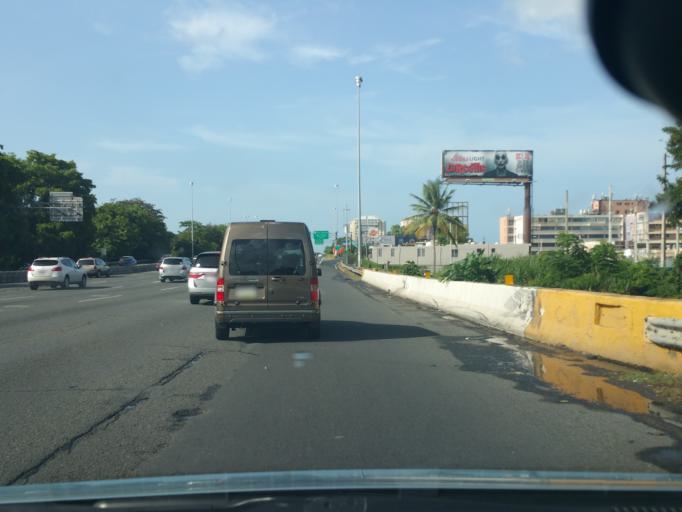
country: PR
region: Catano
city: Catano
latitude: 18.4099
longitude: -66.0697
